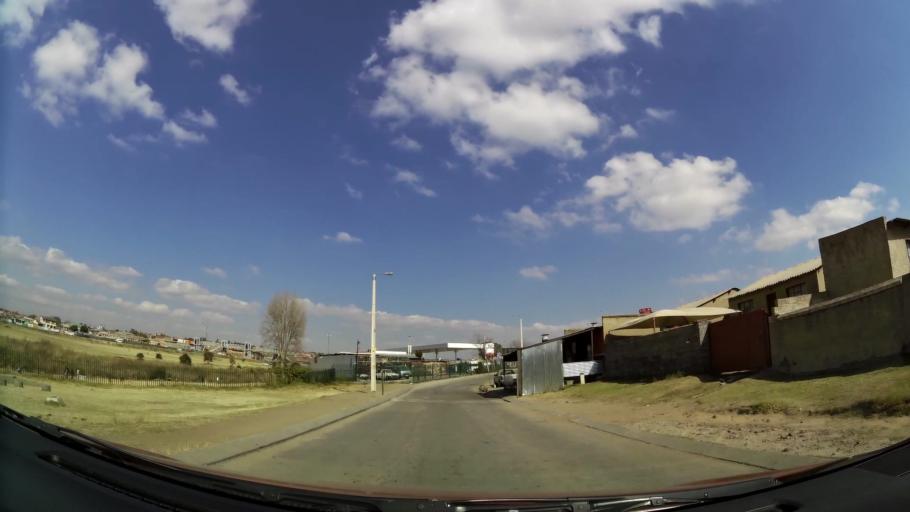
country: ZA
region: Gauteng
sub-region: Ekurhuleni Metropolitan Municipality
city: Tembisa
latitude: -26.0167
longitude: 28.1998
